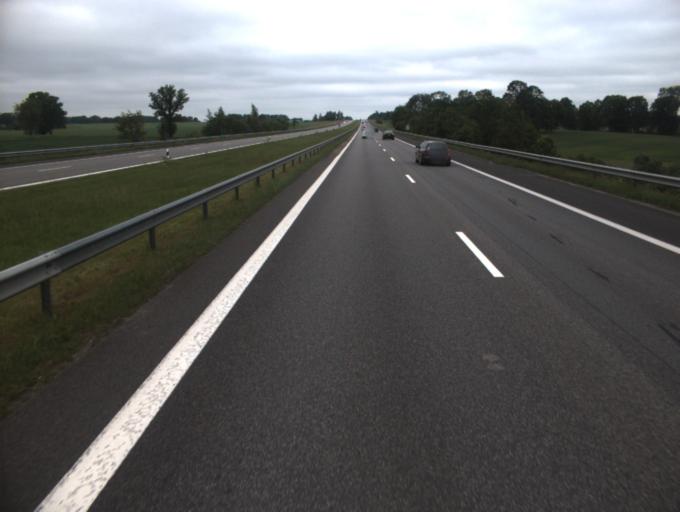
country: LT
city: Ariogala
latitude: 55.2889
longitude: 23.2939
